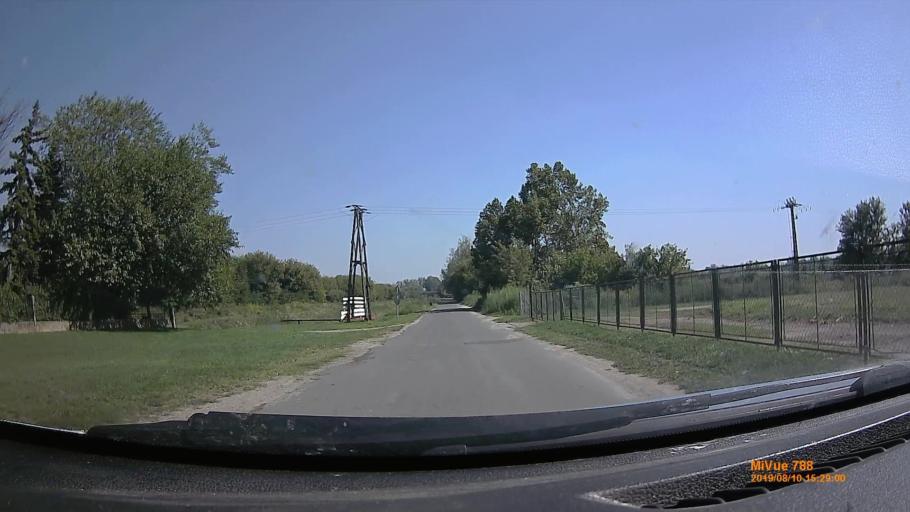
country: HU
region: Somogy
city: Balatonfenyves
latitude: 46.7081
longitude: 17.4800
